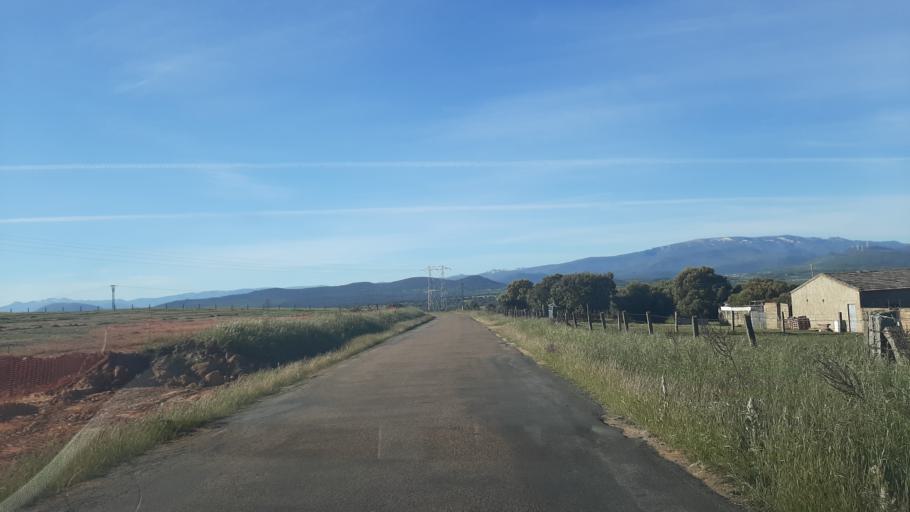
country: ES
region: Castille and Leon
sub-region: Provincia de Salamanca
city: Guijuelo
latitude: 40.5496
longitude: -5.6660
